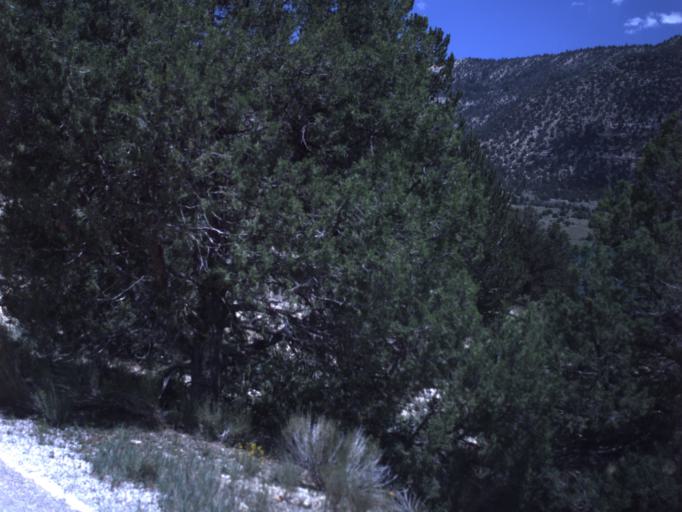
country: US
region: Utah
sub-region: Emery County
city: Orangeville
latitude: 39.3106
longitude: -111.2859
